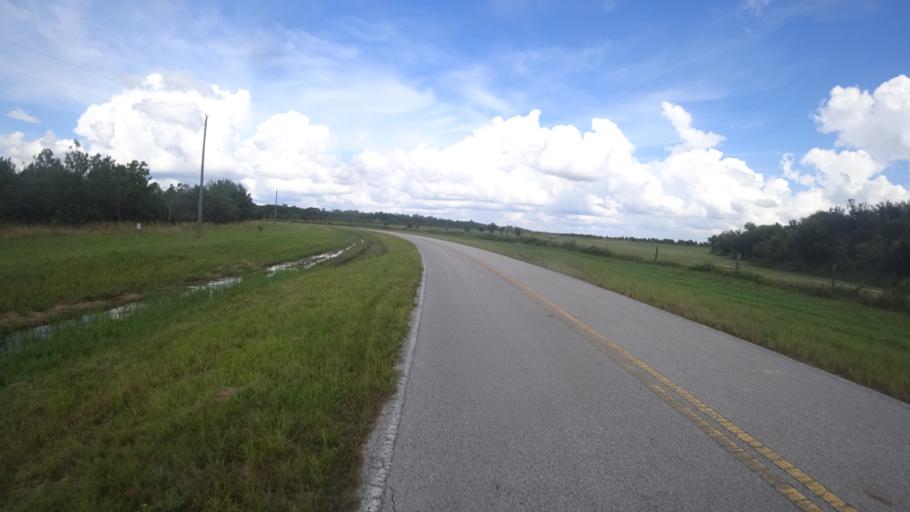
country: US
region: Florida
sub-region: Hillsborough County
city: Wimauma
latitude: 27.5876
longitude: -82.1808
